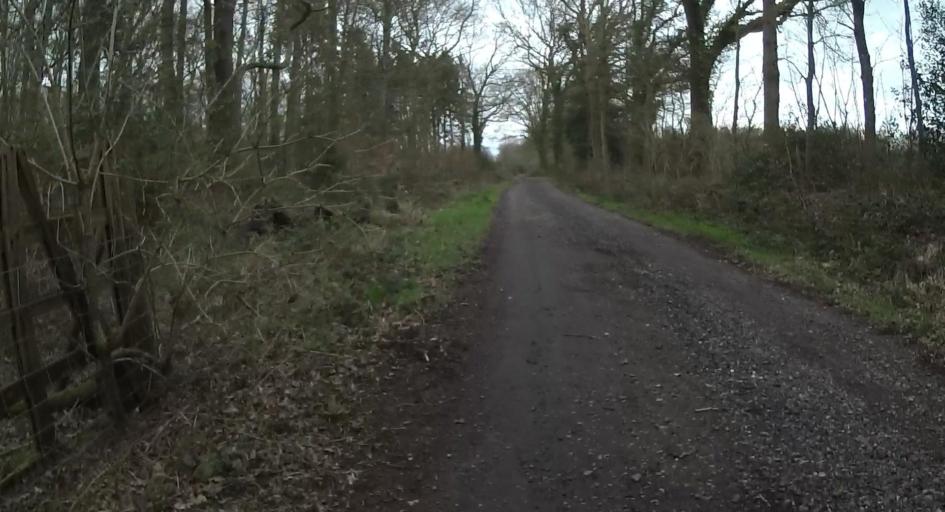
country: GB
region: England
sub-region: Hampshire
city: Basingstoke
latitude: 51.1938
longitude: -1.0553
